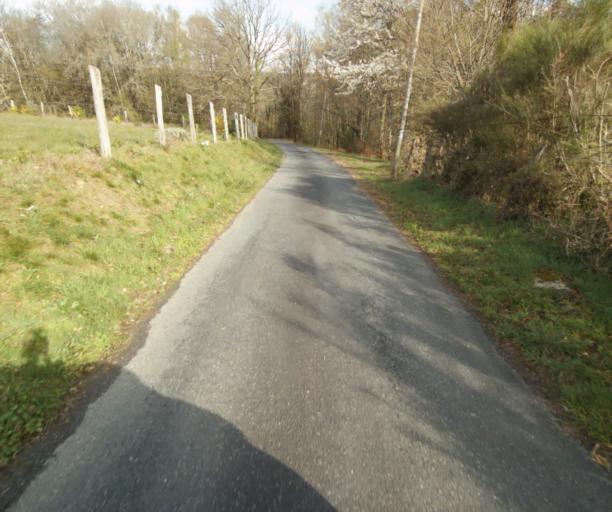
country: FR
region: Limousin
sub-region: Departement de la Correze
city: Correze
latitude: 45.3420
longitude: 1.8316
